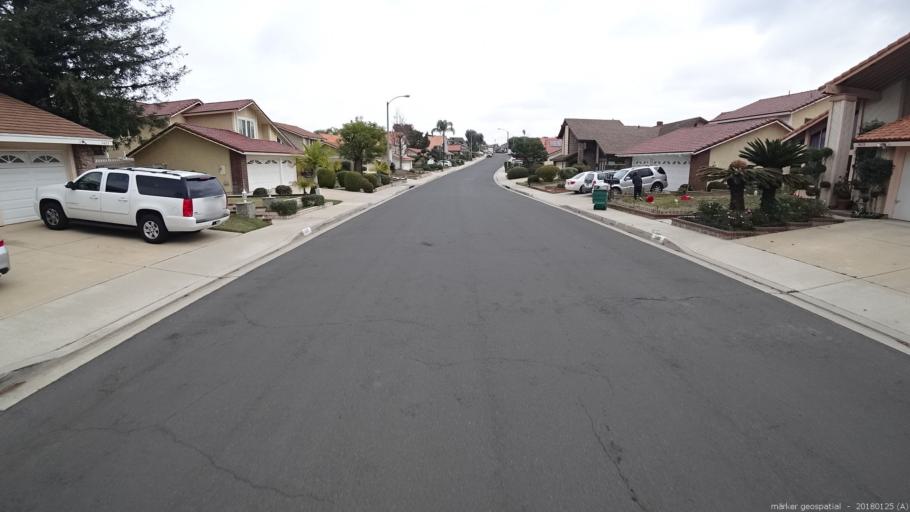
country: US
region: California
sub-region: Los Angeles County
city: Walnut
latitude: 33.9629
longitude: -117.8386
